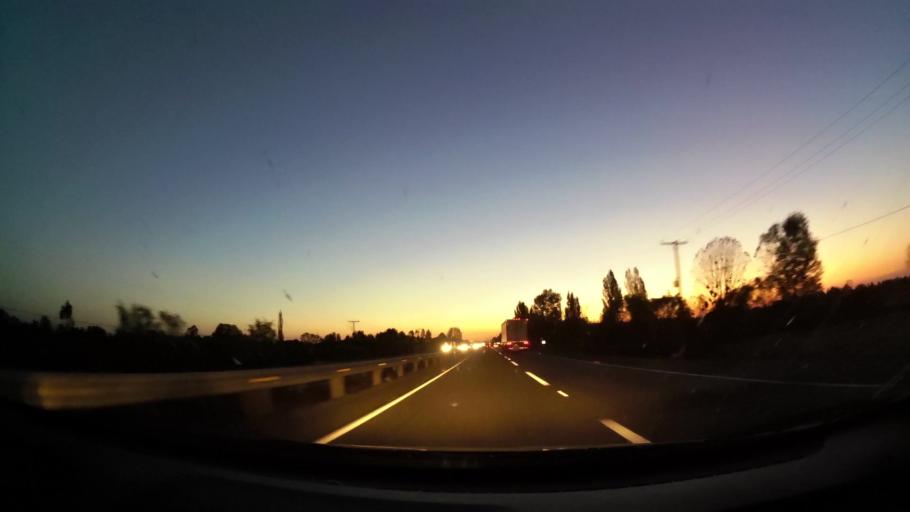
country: CL
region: Biobio
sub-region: Provincia de Nuble
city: San Carlos
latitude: -36.3555
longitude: -71.8686
